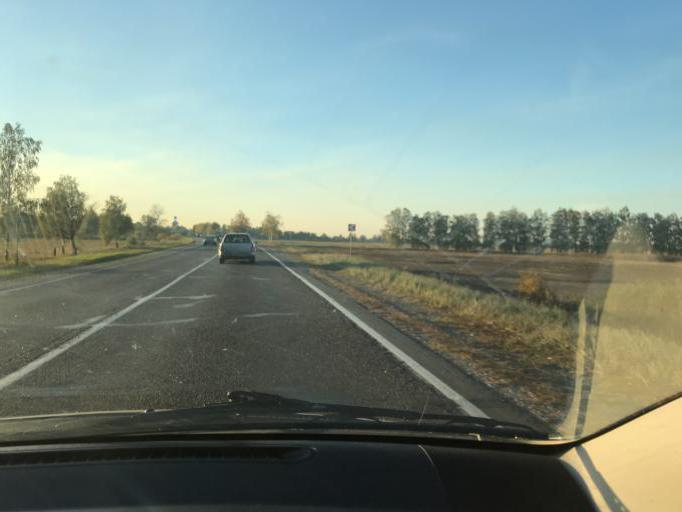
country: BY
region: Brest
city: Pinsk
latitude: 52.0717
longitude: 26.1746
